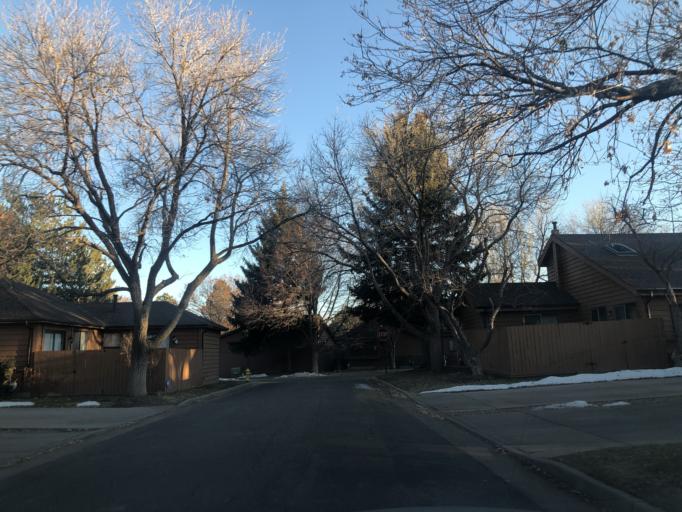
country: US
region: Colorado
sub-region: Adams County
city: Aurora
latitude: 39.7178
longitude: -104.8170
